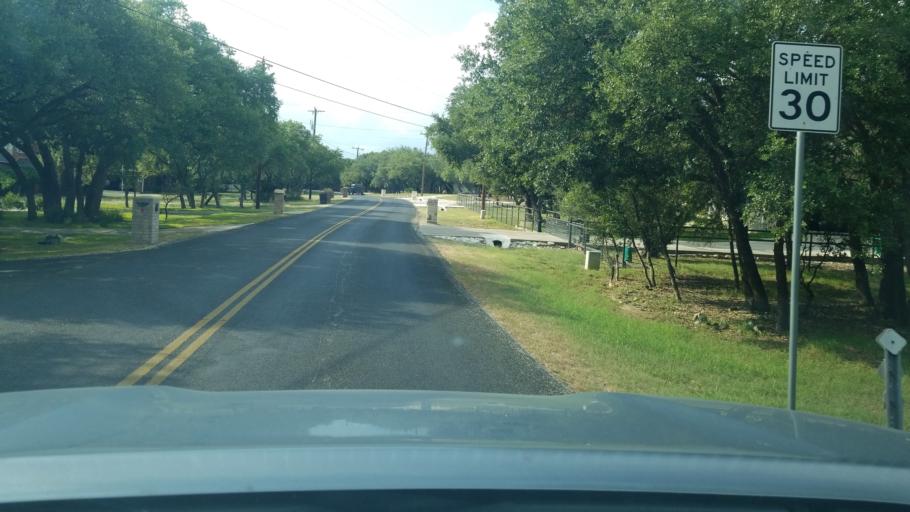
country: US
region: Texas
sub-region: Bexar County
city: Timberwood Park
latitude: 29.6866
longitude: -98.4799
